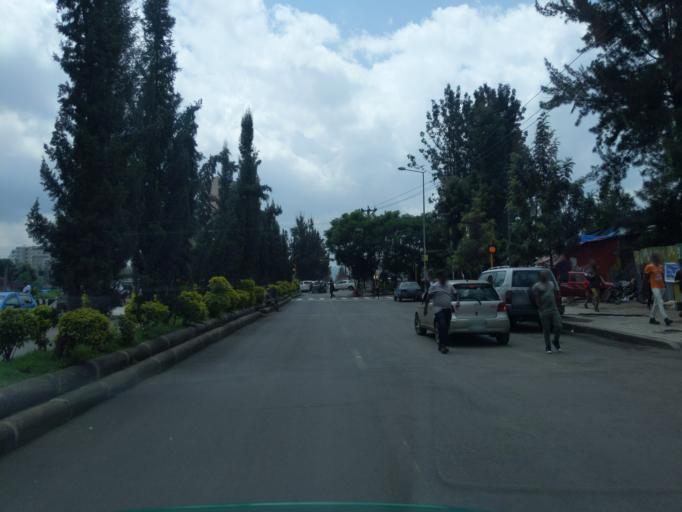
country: ET
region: Adis Abeba
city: Addis Ababa
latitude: 9.0154
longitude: 38.7701
